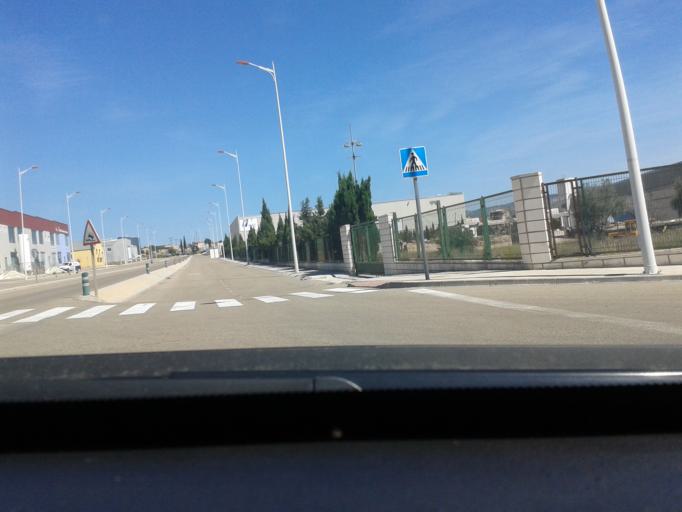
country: ES
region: Castille-La Mancha
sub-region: Provincia de Albacete
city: Caudete
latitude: 38.7123
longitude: -0.9703
